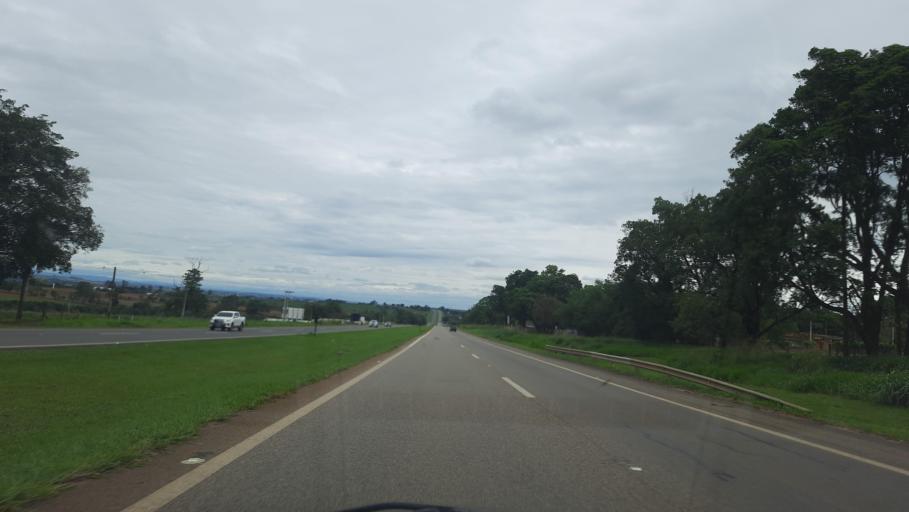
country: BR
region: Sao Paulo
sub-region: Moji-Guacu
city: Mogi-Gaucu
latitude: -22.2290
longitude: -46.9788
